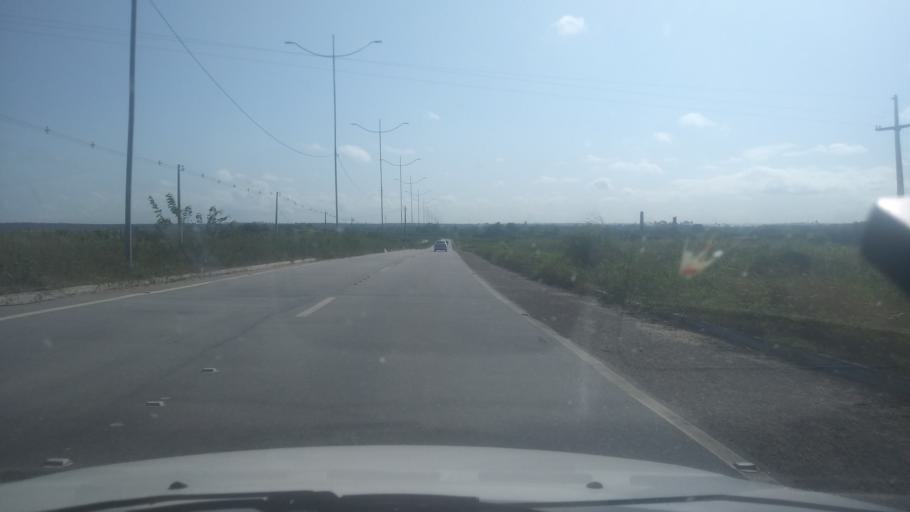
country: BR
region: Rio Grande do Norte
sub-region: Macaiba
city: Macaiba
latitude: -5.8193
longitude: -35.3655
